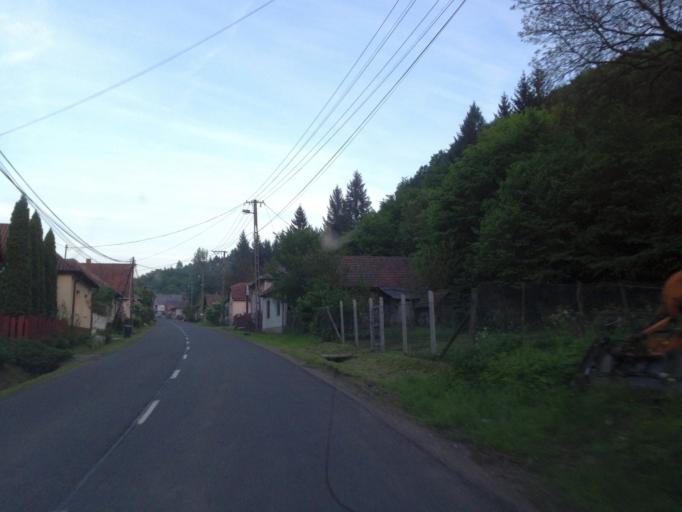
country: HU
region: Nograd
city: Batonyterenye
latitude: 47.9030
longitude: 19.8101
